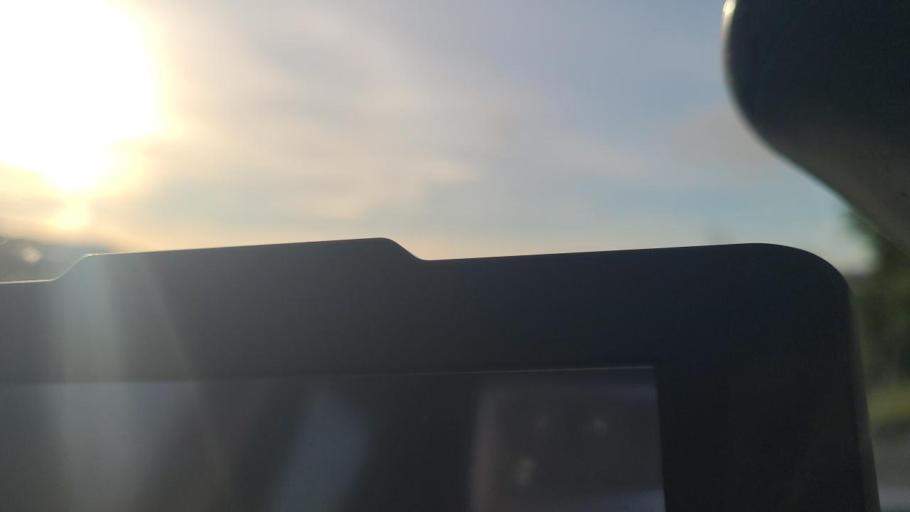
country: NZ
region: Southland
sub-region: Southland District
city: Winton
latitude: -46.2051
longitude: 168.3541
